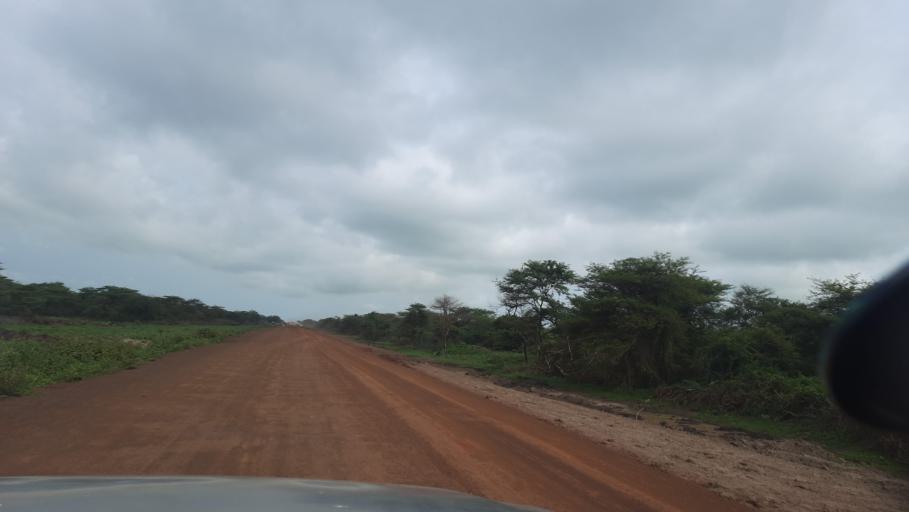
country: ET
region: Gambela
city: Gambela
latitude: 8.3449
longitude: 33.9052
